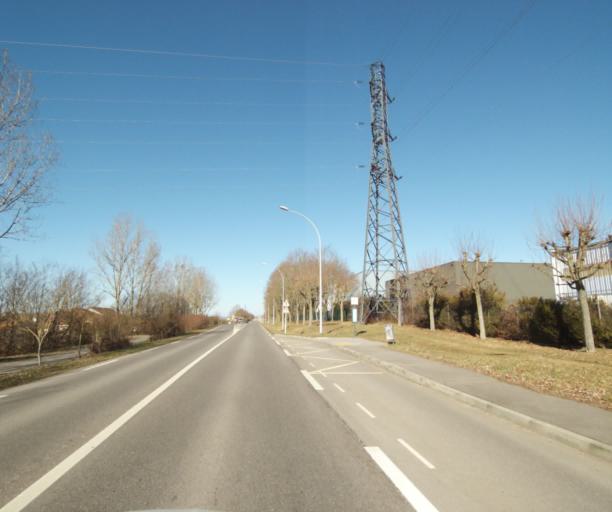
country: FR
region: Lorraine
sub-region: Departement de Meurthe-et-Moselle
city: Heillecourt
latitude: 48.6513
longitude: 6.2080
